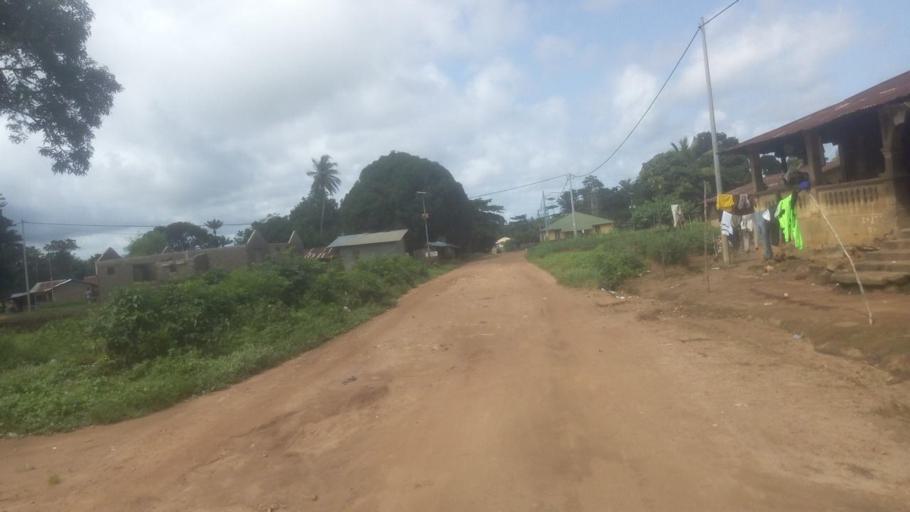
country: SL
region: Northern Province
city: Tintafor
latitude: 8.6399
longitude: -13.2227
